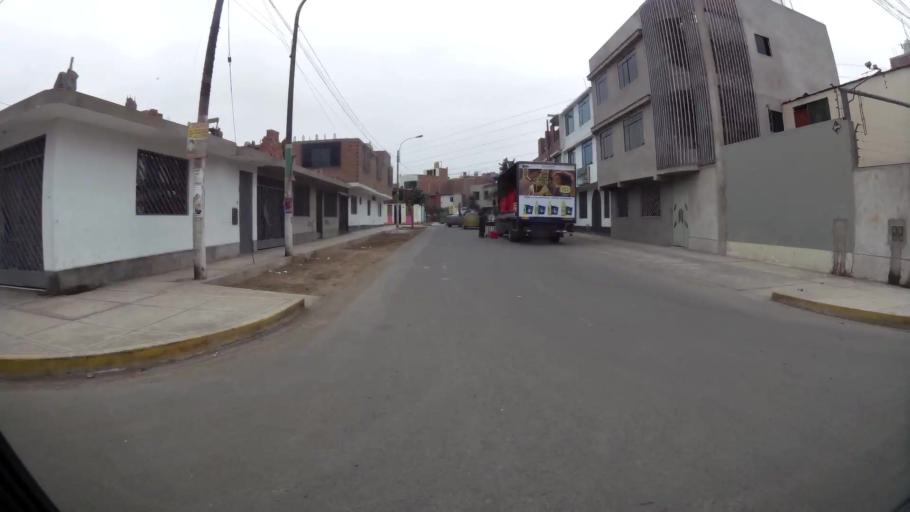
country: PE
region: Lima
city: Ventanilla
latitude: -11.9322
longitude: -77.0835
